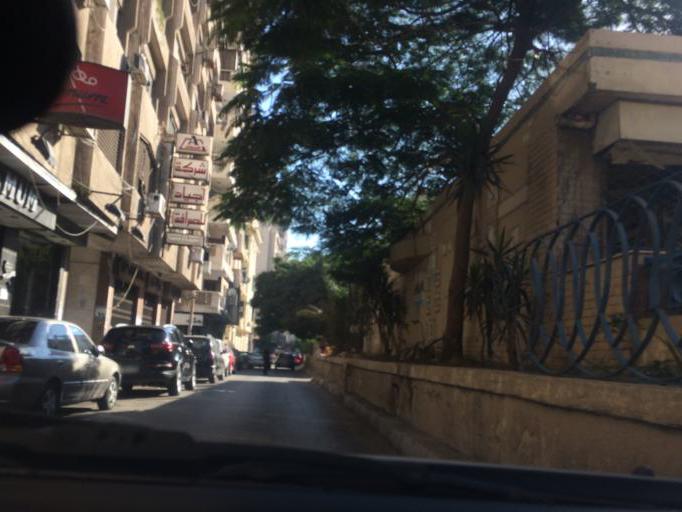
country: EG
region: Alexandria
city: Alexandria
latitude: 31.2310
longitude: 29.9552
